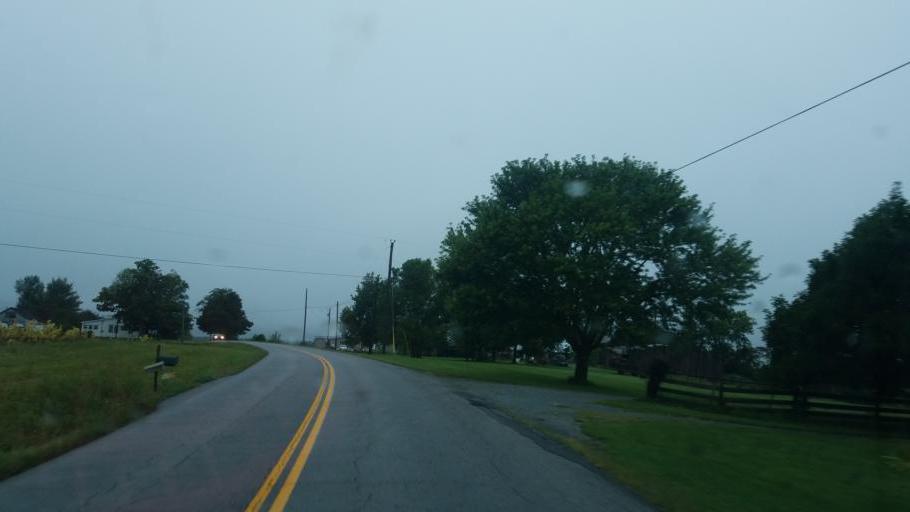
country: US
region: Kentucky
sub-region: Fleming County
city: Flemingsburg
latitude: 38.4150
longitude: -83.6727
